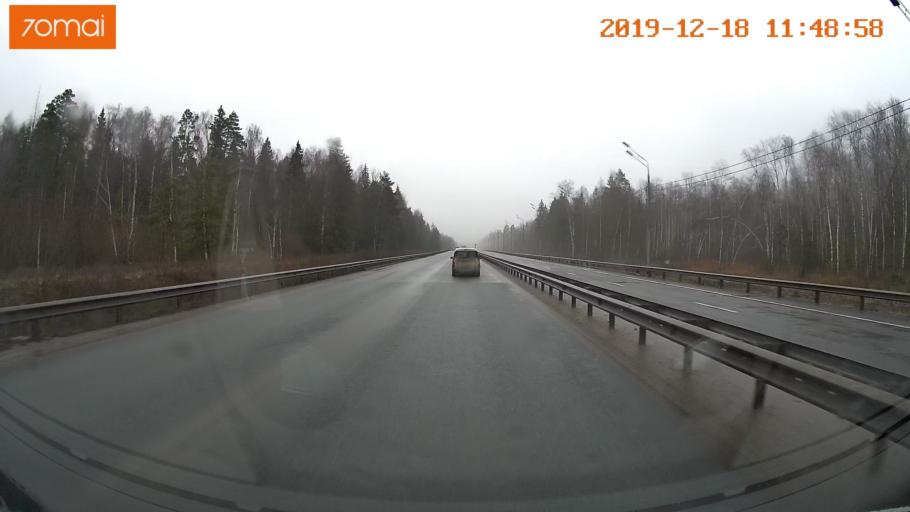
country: RU
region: Moskovskaya
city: Yershovo
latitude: 55.7733
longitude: 36.9079
